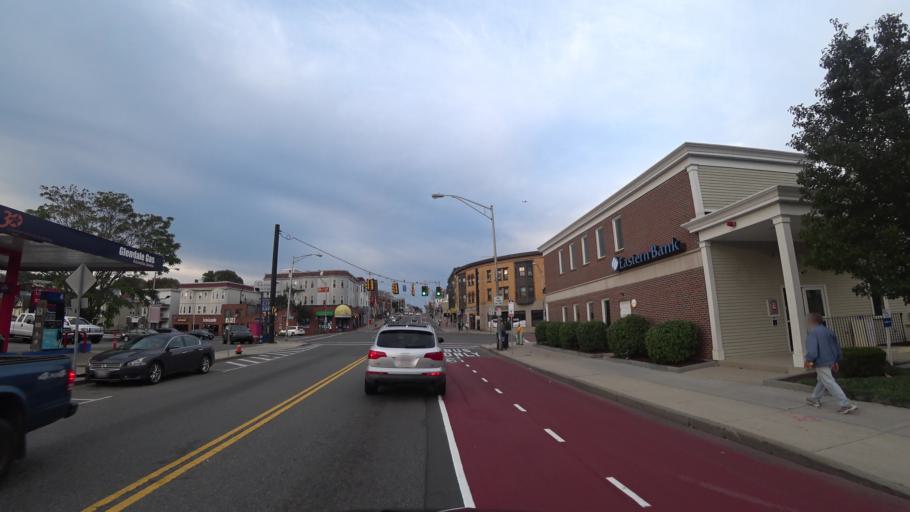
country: US
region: Massachusetts
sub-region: Middlesex County
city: Everett
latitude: 42.4157
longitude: -71.0478
